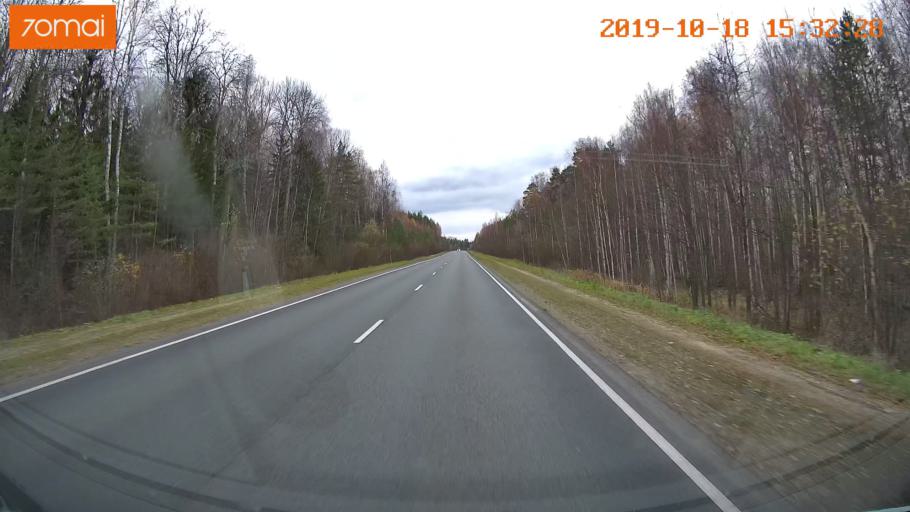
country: RU
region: Vladimir
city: Anopino
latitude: 55.8266
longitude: 40.6530
